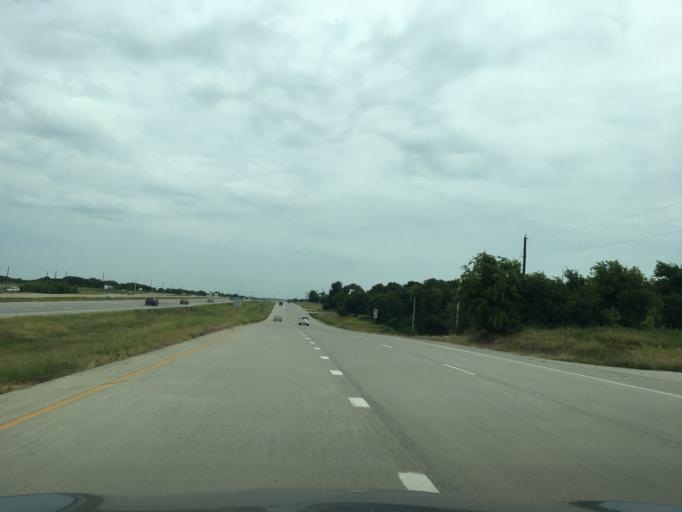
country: US
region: Texas
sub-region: Collin County
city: Melissa
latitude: 33.2758
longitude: -96.5924
